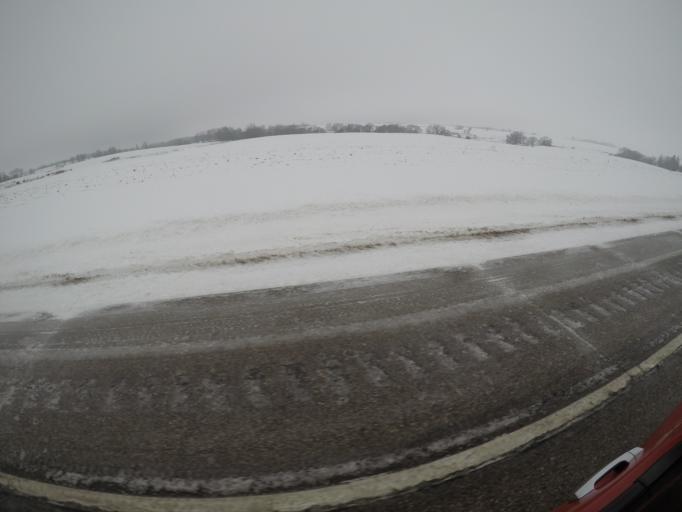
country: US
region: Minnesota
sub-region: Goodhue County
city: Wanamingo
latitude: 44.3375
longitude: -92.7502
